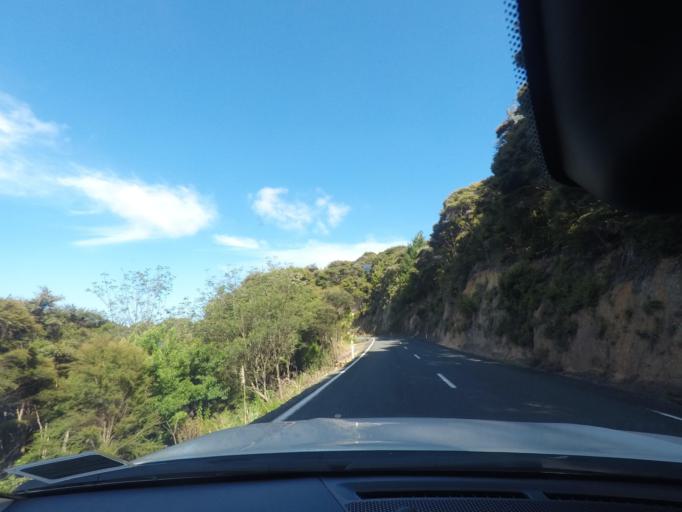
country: NZ
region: Northland
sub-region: Whangarei
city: Ngunguru
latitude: -35.6715
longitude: 174.4590
